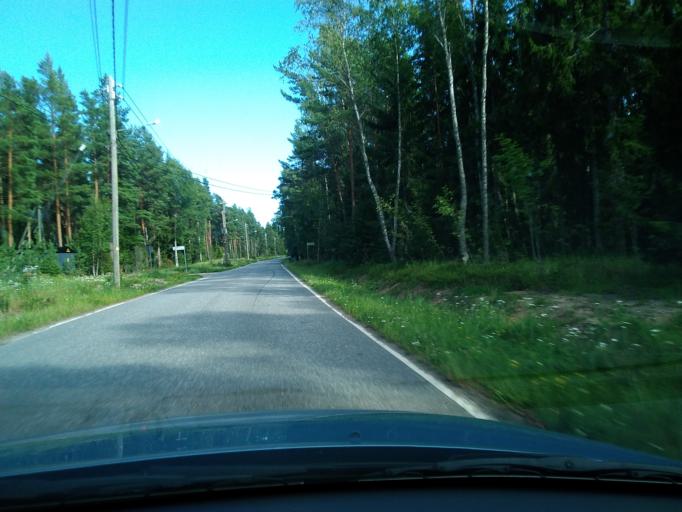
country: FI
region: Uusimaa
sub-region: Raaseporin
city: Hanko
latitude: 59.8337
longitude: 23.1211
